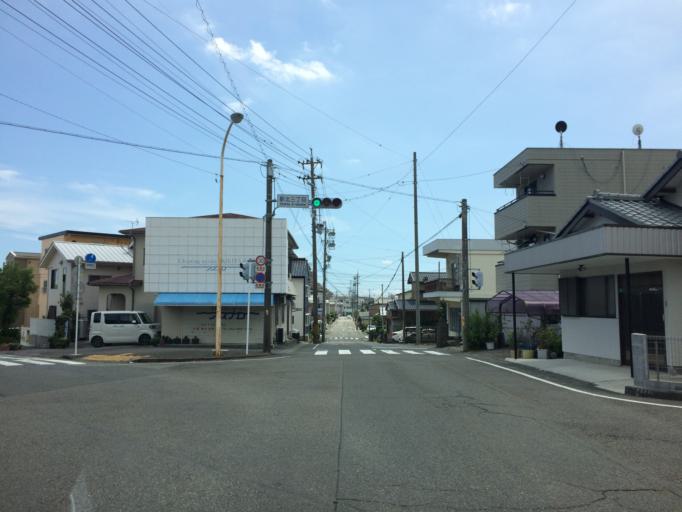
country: JP
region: Shizuoka
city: Yaizu
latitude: 34.8765
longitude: 138.3156
